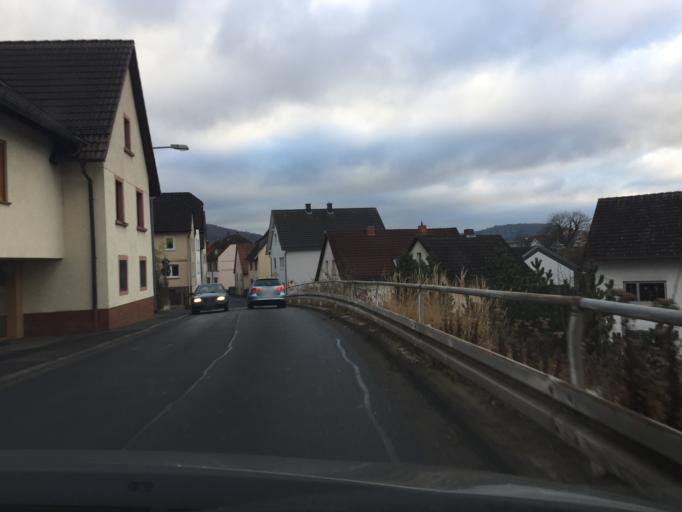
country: DE
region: Bavaria
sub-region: Regierungsbezirk Unterfranken
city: Goldbach
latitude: 50.0018
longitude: 9.1808
